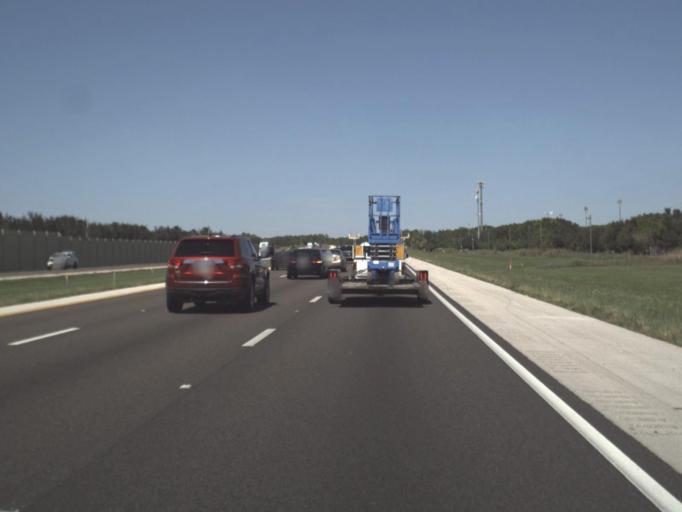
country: US
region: Florida
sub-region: Collier County
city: Vineyards
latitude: 26.2366
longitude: -81.7364
